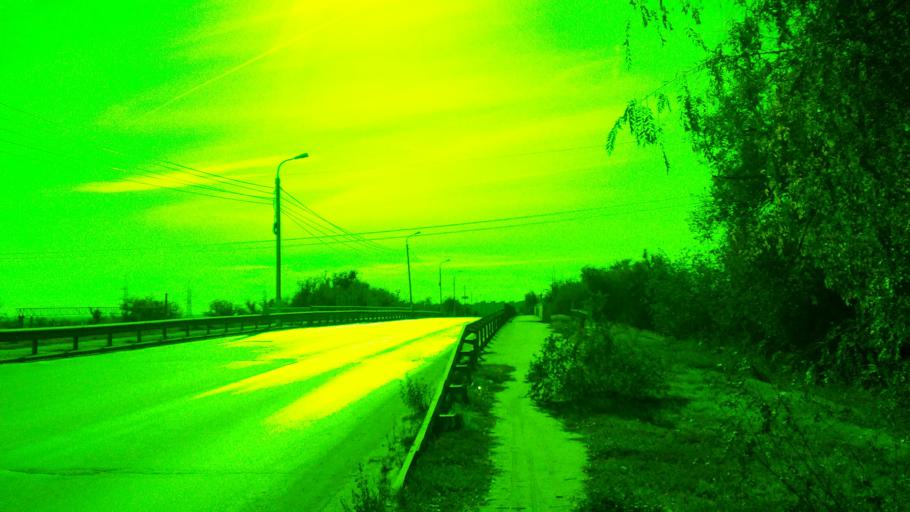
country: RU
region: Volgograd
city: Vodstroy
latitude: 48.8347
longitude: 44.6452
